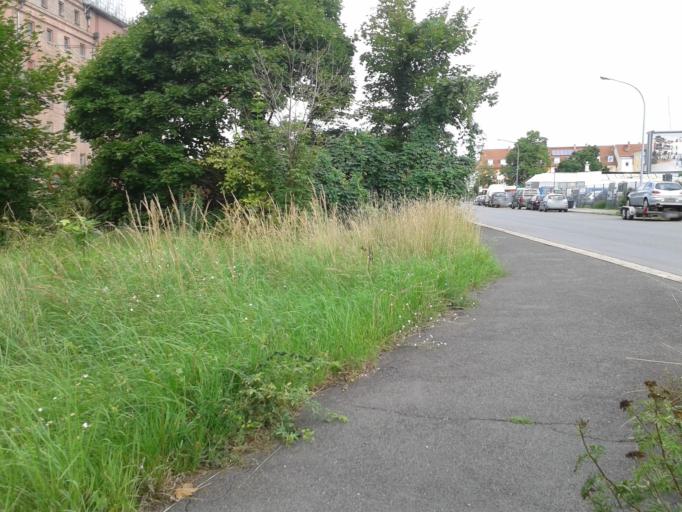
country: DE
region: Bavaria
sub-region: Upper Franconia
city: Bamberg
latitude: 49.8864
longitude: 10.9159
